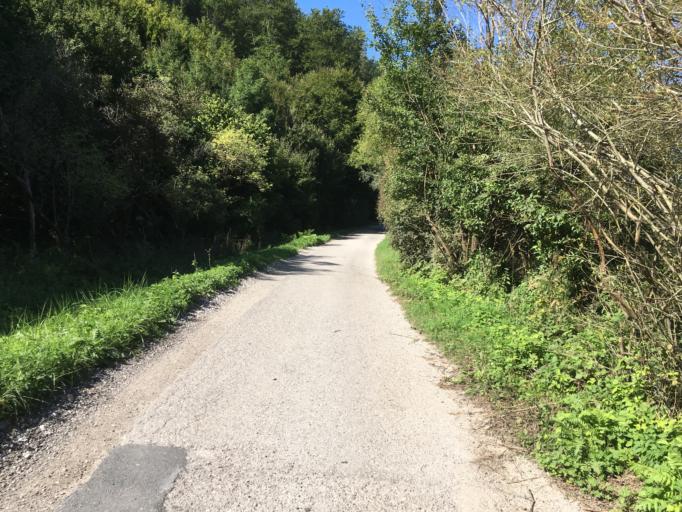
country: SK
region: Trenciansky
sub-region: Okres Povazska Bystrica
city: Povazska Bystrica
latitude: 49.0253
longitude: 18.4371
